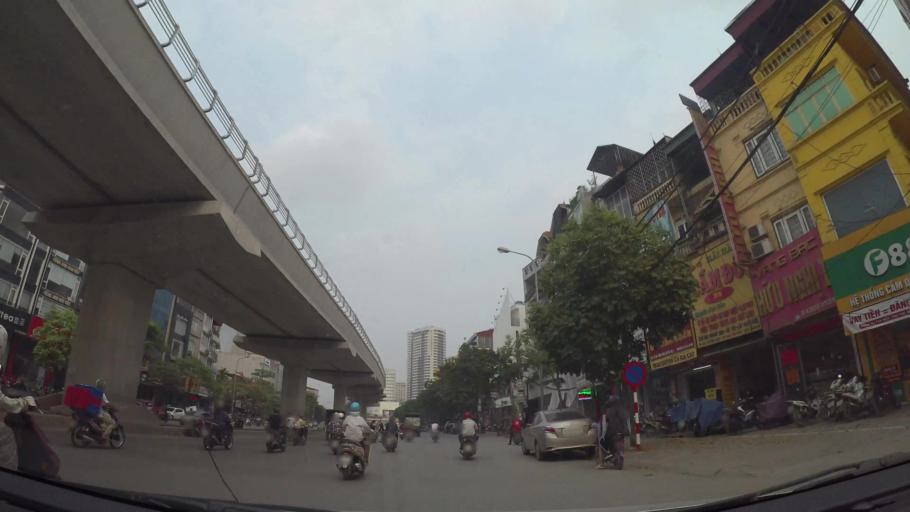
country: VN
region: Ha Noi
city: Cau Dien
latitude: 21.0366
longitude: 105.7773
